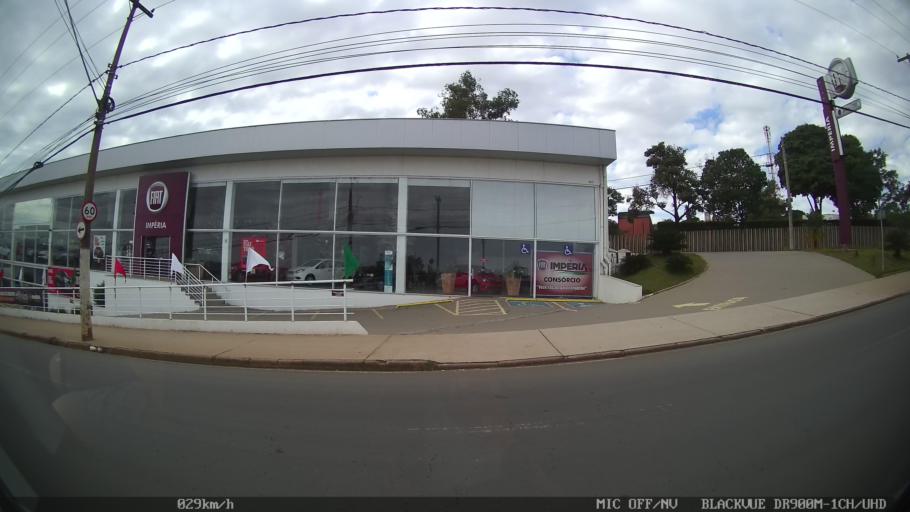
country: BR
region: Sao Paulo
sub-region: Limeira
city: Limeira
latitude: -22.5515
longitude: -47.3821
